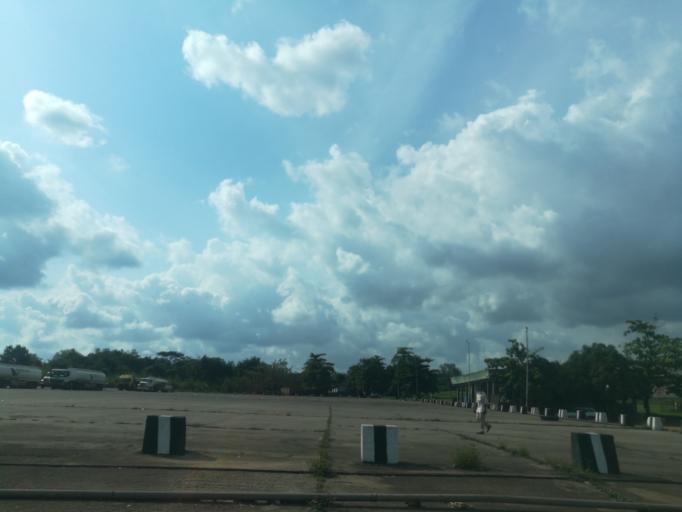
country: NG
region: Oyo
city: Ibadan
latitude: 7.3918
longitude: 3.8192
